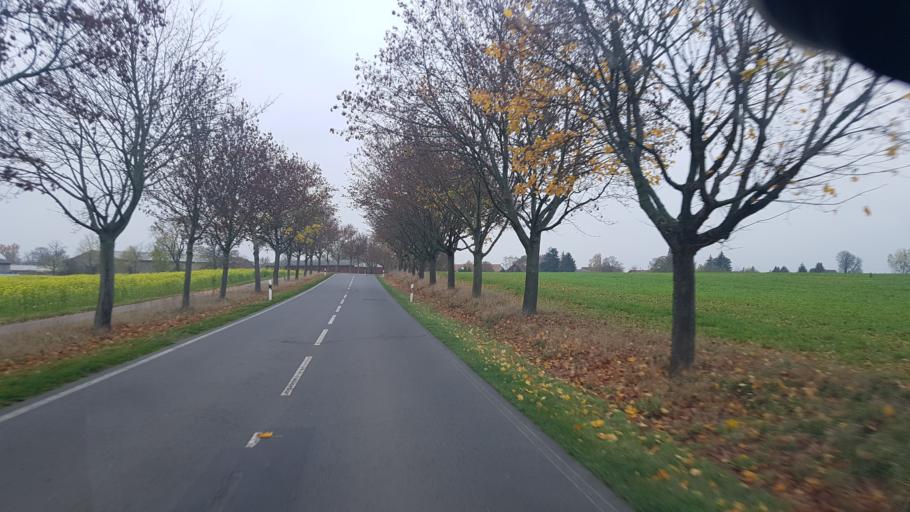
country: DE
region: Brandenburg
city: Schonermark
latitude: 52.9274
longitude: 13.1154
